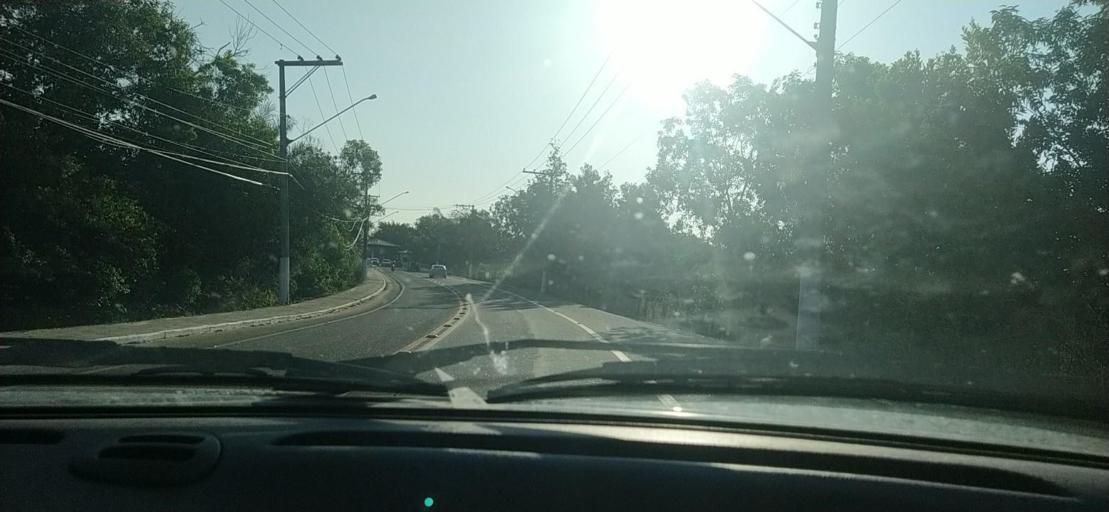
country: BR
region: Espirito Santo
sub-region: Conceicao Da Barra
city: Conceicao da Barra
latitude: -18.5670
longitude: -39.7452
